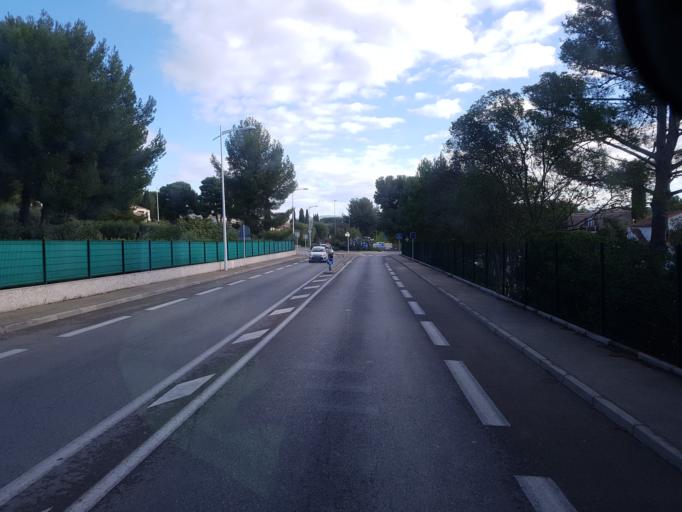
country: FR
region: Provence-Alpes-Cote d'Azur
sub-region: Departement du Var
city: Saint-Cyr-sur-Mer
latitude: 43.1823
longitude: 5.6845
